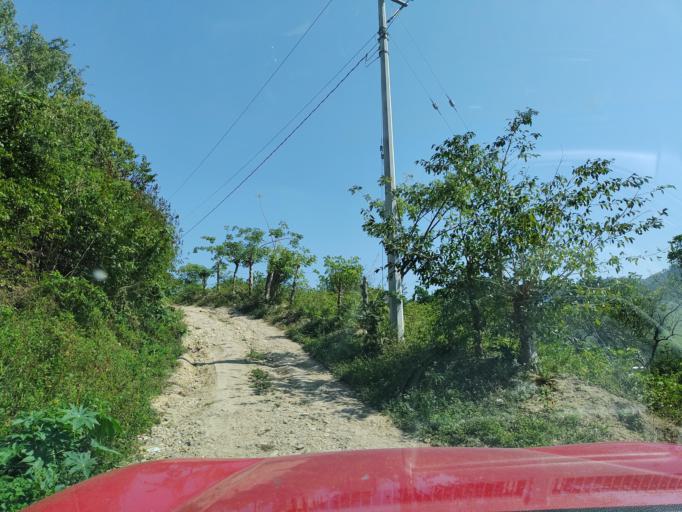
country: MX
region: Veracruz
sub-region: Papantla
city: Polutla
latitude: 20.5172
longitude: -97.2422
